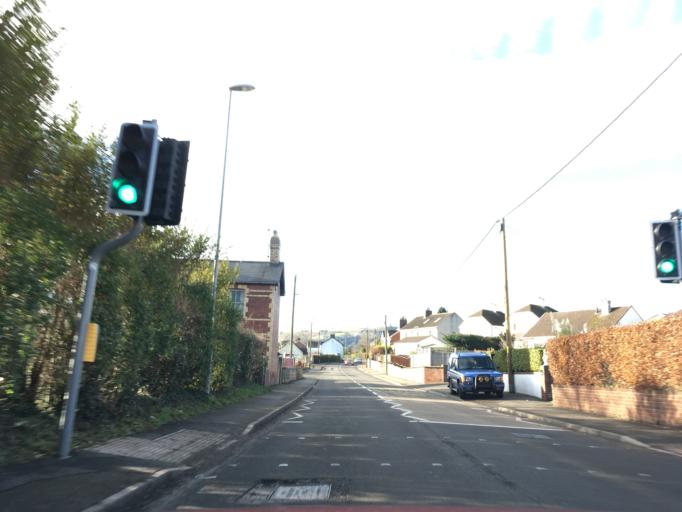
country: GB
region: Wales
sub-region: Torfaen County Borough
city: New Inn
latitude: 51.7212
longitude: -2.9831
